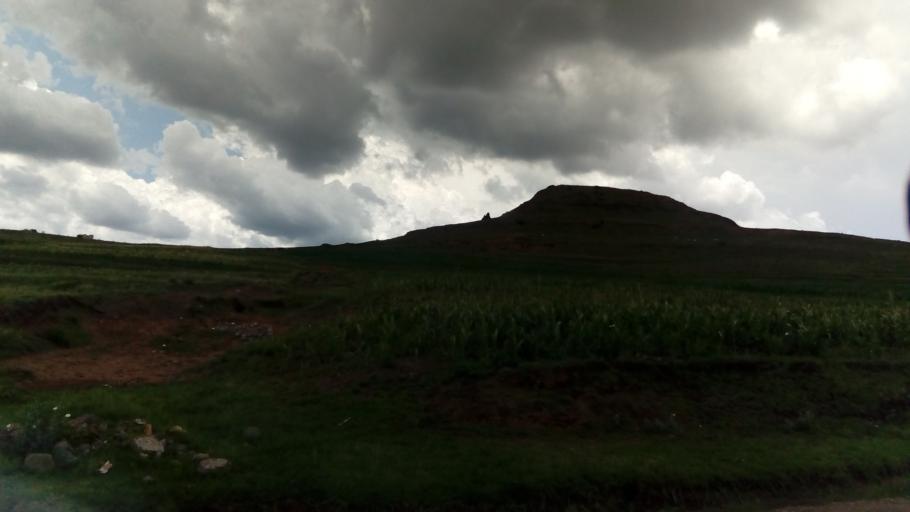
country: LS
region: Berea
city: Teyateyaneng
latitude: -29.2152
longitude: 27.8637
